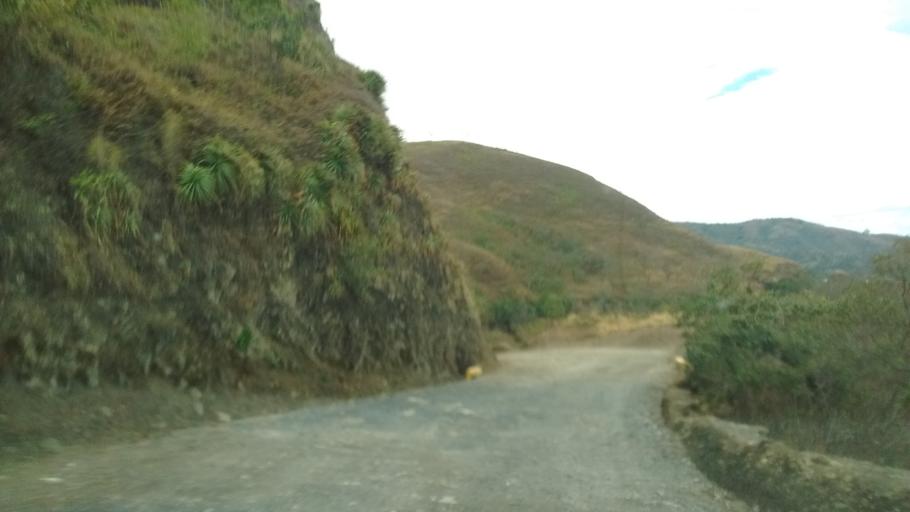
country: CO
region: Cauca
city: Almaguer
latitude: 1.8424
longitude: -76.9090
